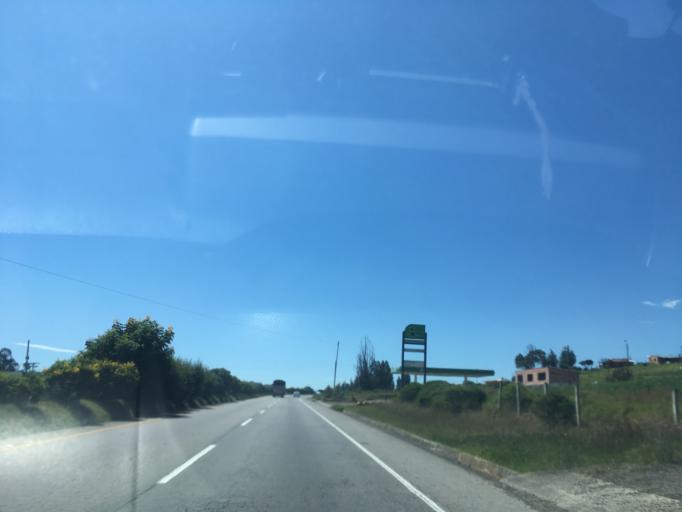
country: CO
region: Boyaca
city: Tuta
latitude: 5.6930
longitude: -73.2507
